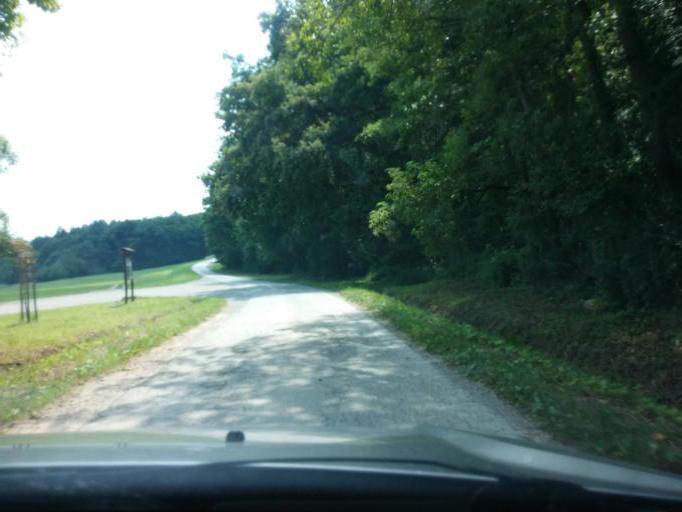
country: HU
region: Somogy
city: Kaposvar
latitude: 46.2447
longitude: 17.7748
